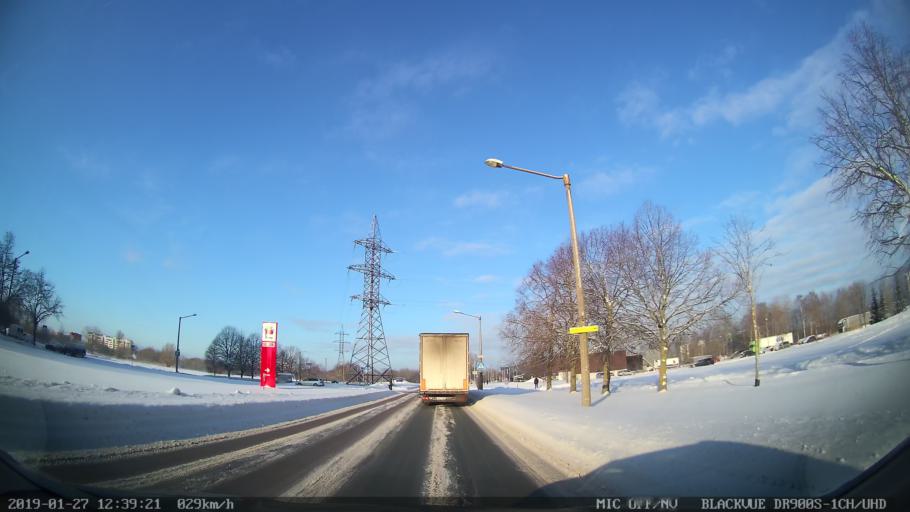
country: EE
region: Harju
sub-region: Tallinna linn
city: Kose
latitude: 59.4414
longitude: 24.8245
